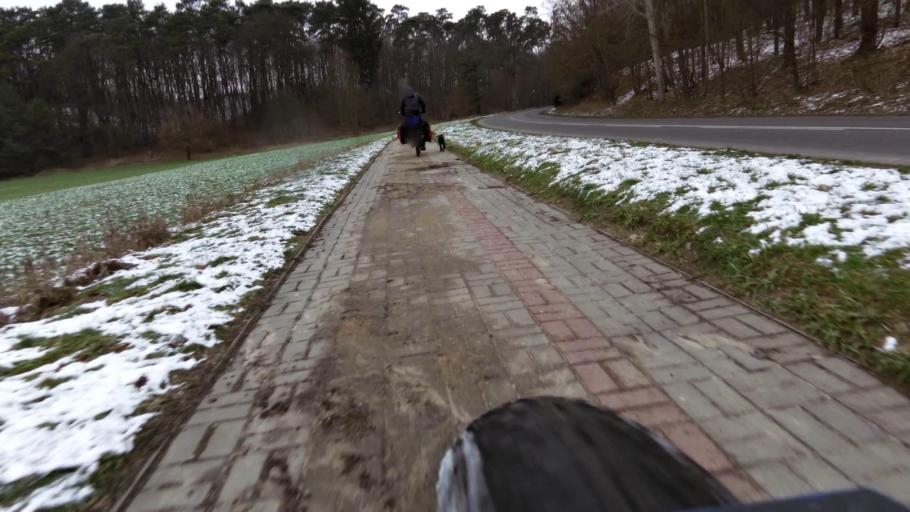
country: PL
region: West Pomeranian Voivodeship
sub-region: Powiat walecki
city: Miroslawiec
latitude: 53.3559
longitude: 16.0852
